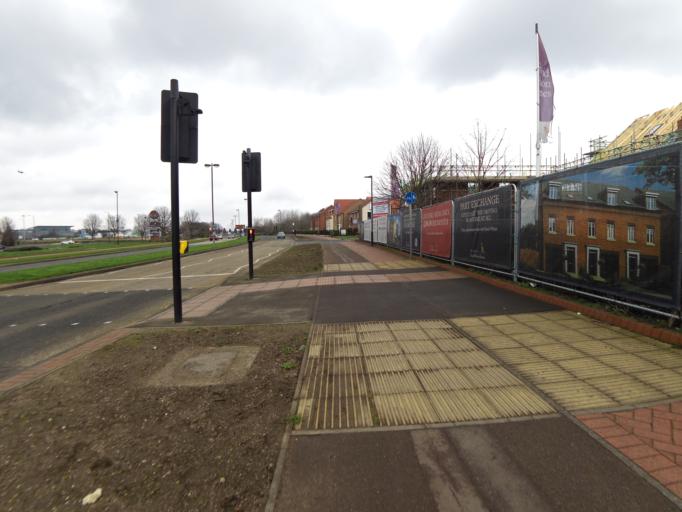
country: GB
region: England
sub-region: Doncaster
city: Doncaster
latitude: 53.5119
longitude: -1.1022
